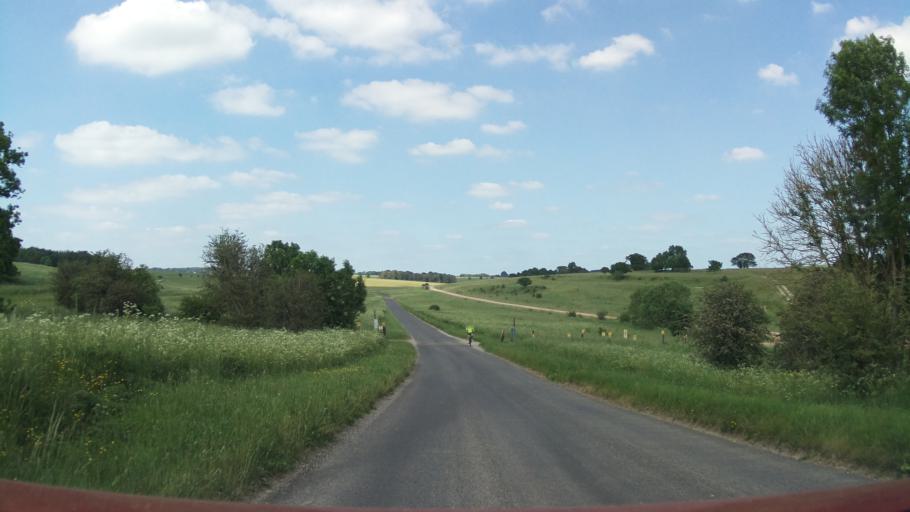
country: GB
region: England
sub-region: Wiltshire
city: Milston
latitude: 51.2605
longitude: -1.7286
